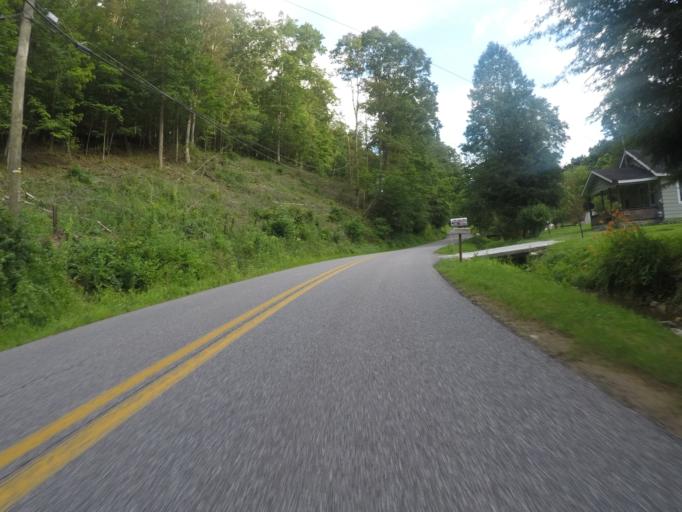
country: US
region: West Virginia
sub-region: Cabell County
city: Pea Ridge
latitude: 38.3975
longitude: -82.3617
